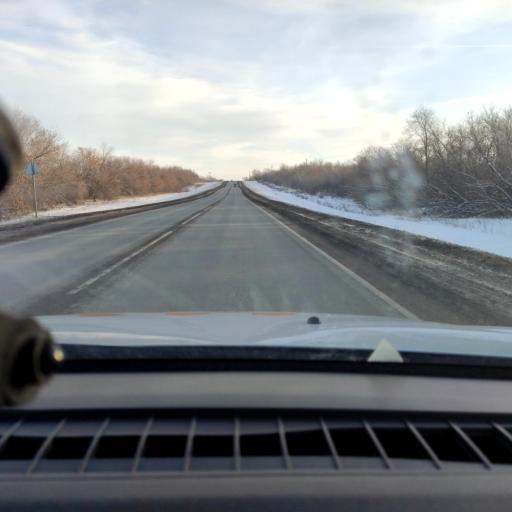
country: RU
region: Samara
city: Samara
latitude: 53.0728
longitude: 50.1724
